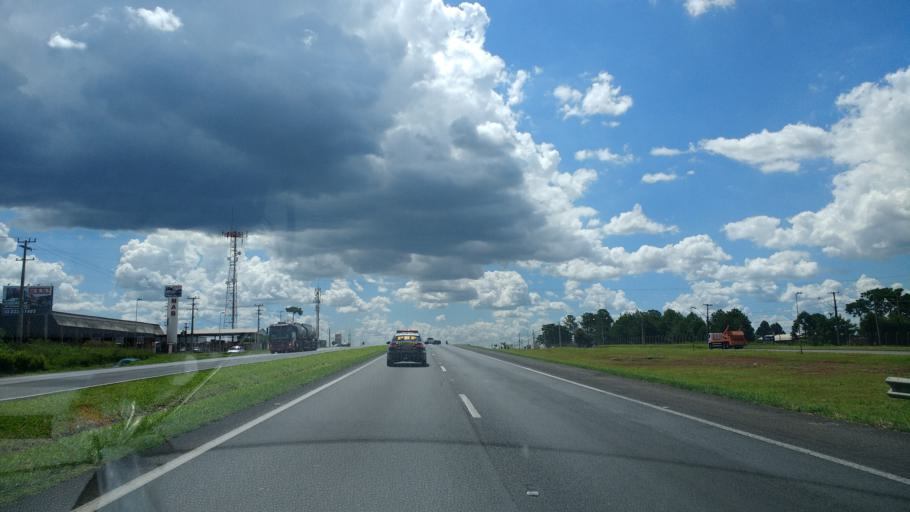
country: BR
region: Parana
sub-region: Ponta Grossa
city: Ponta Grossa
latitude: -25.1810
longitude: -50.0948
